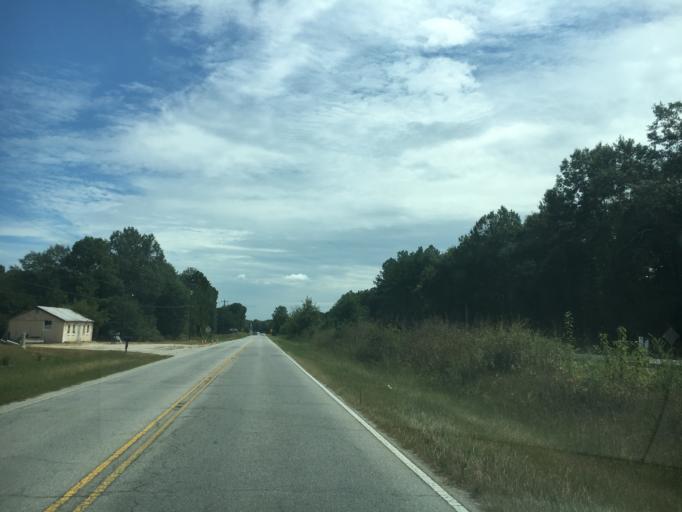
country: US
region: South Carolina
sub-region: Laurens County
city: Laurens
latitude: 34.5383
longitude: -82.0635
